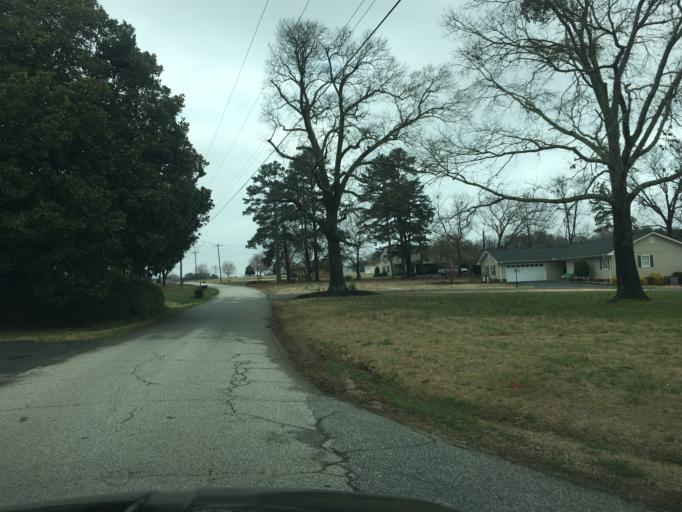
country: US
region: South Carolina
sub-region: Spartanburg County
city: Inman Mills
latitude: 35.0222
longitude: -82.1110
